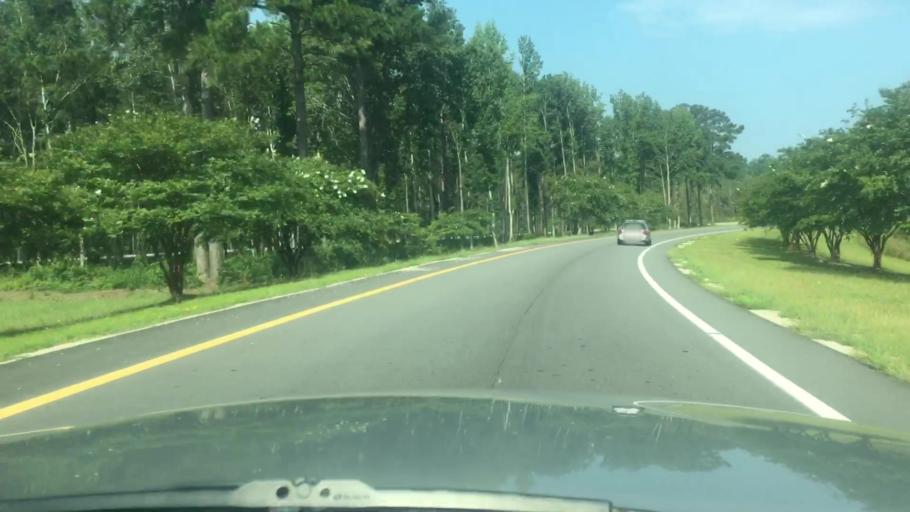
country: US
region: North Carolina
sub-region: Cumberland County
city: Fayetteville
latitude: 34.9795
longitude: -78.8563
